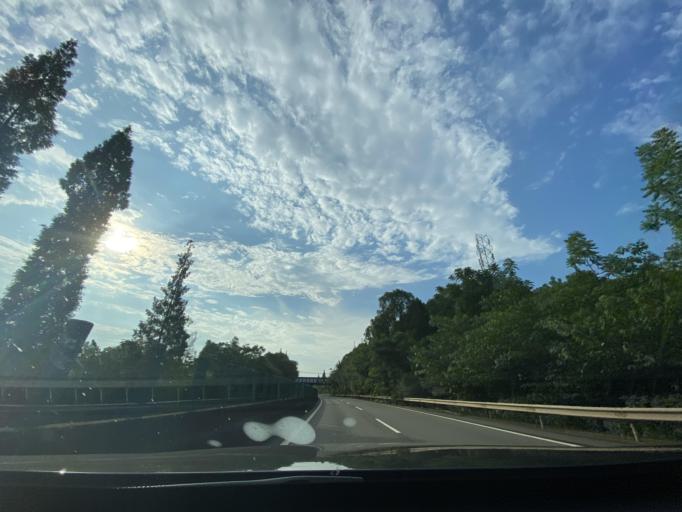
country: CN
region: Sichuan
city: Jiancheng
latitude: 30.2915
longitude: 104.5866
